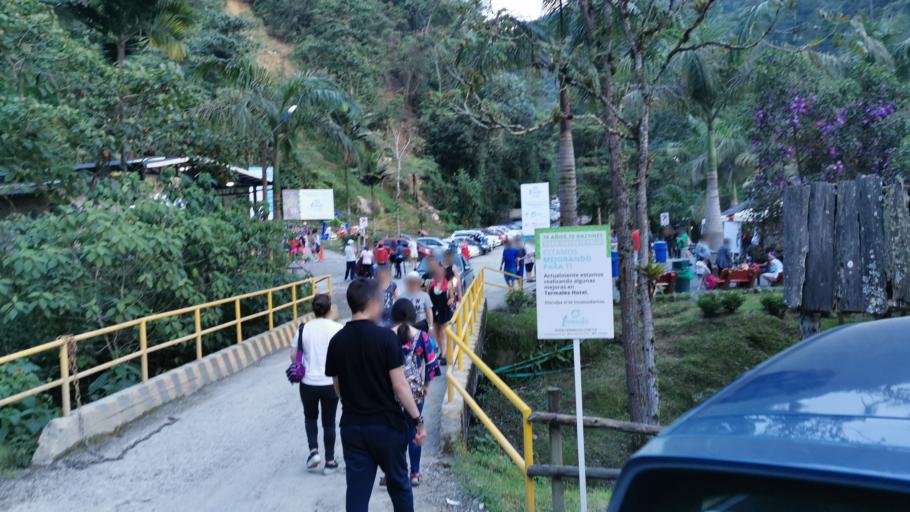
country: CO
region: Risaralda
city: Santa Rosa de Cabal
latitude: 4.8430
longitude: -75.5555
